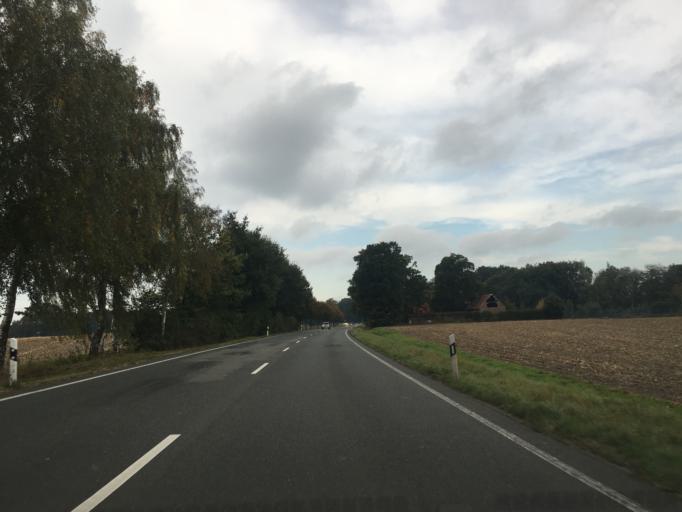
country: DE
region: North Rhine-Westphalia
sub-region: Regierungsbezirk Munster
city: Schoppingen
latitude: 52.0981
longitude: 7.2119
